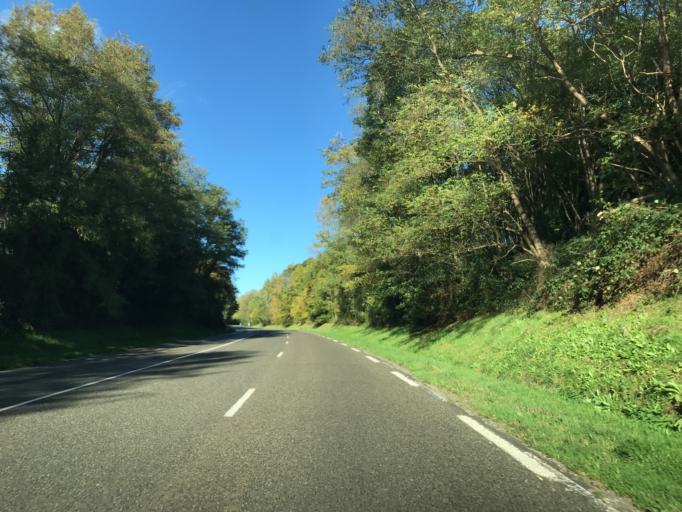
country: FR
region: Haute-Normandie
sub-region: Departement de l'Eure
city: Saint-Aubin-sur-Gaillon
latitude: 49.1140
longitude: 1.3014
